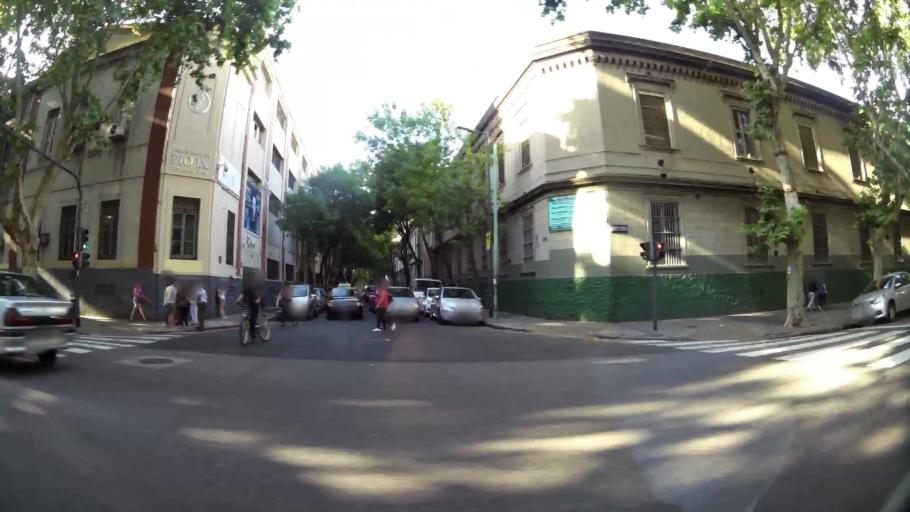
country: AR
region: Buenos Aires F.D.
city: Buenos Aires
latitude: -34.6143
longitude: -58.4217
